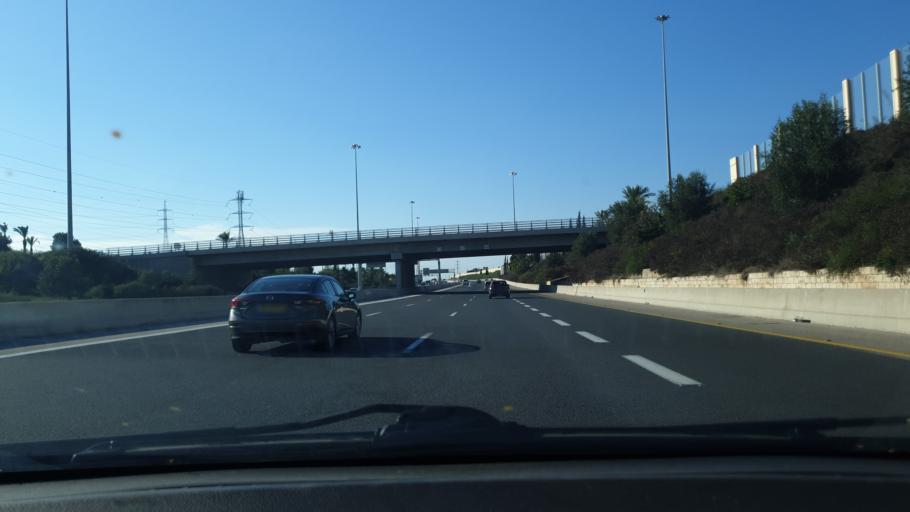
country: IL
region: Central District
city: Rishon LeZiyyon
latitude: 31.9624
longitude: 34.7691
